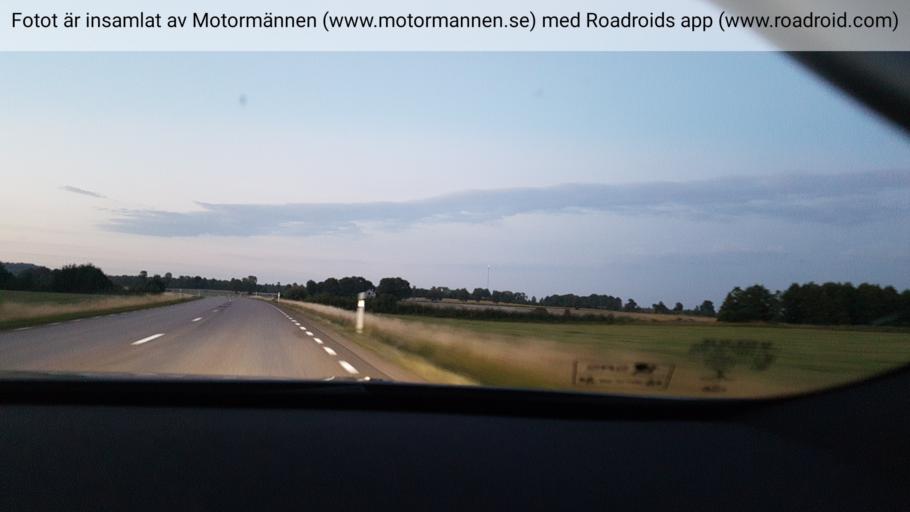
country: SE
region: Vaestra Goetaland
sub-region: Falkopings Kommun
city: Akarp
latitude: 58.2733
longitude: 13.7470
